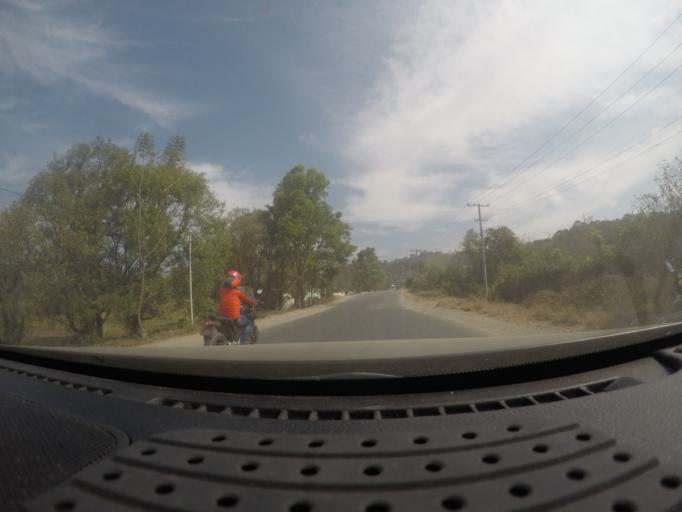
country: MM
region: Shan
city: Taunggyi
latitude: 20.6402
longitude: 96.5891
